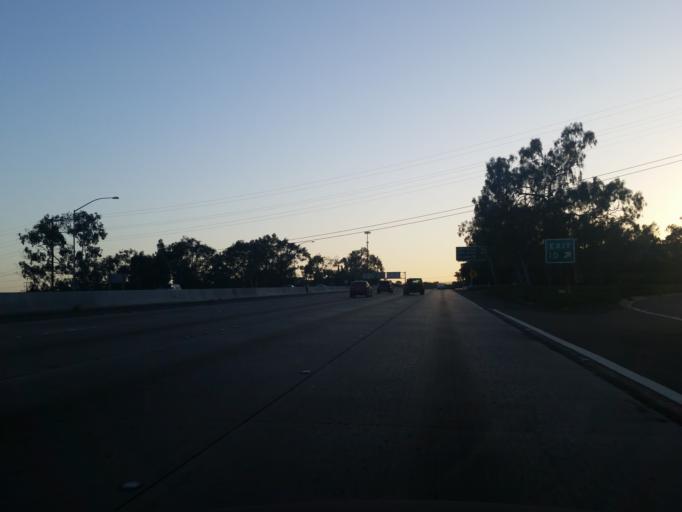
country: US
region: California
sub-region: San Diego County
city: San Diego
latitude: 32.7155
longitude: -117.1243
